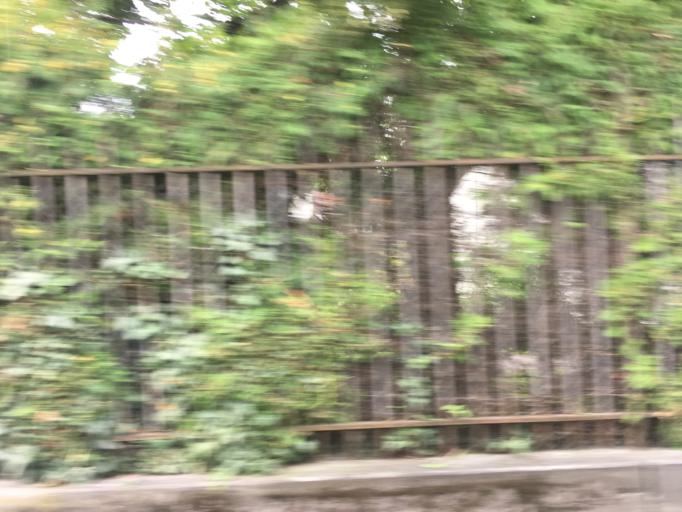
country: CH
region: Bern
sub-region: Thun District
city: Hilterfingen
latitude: 46.7439
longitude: 7.6471
